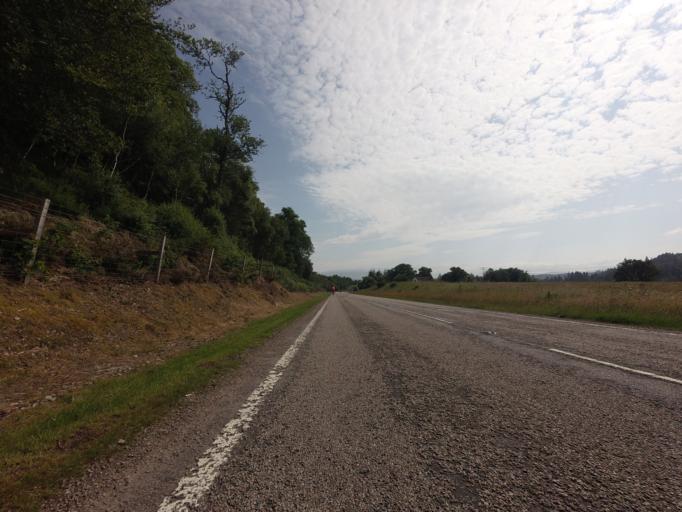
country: GB
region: Scotland
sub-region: Highland
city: Evanton
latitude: 57.9300
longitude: -4.4014
